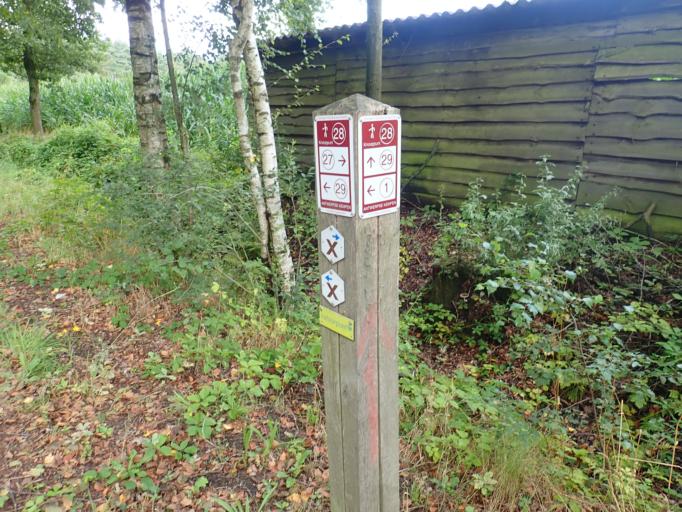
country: BE
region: Flanders
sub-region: Provincie Antwerpen
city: Lille
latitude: 51.2665
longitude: 4.8175
